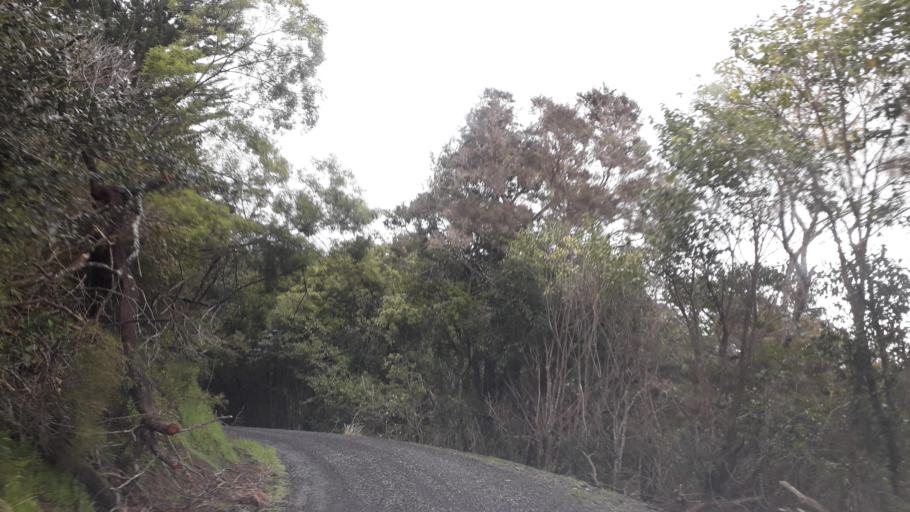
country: NZ
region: Northland
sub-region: Far North District
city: Waimate North
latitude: -35.3144
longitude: 173.5676
